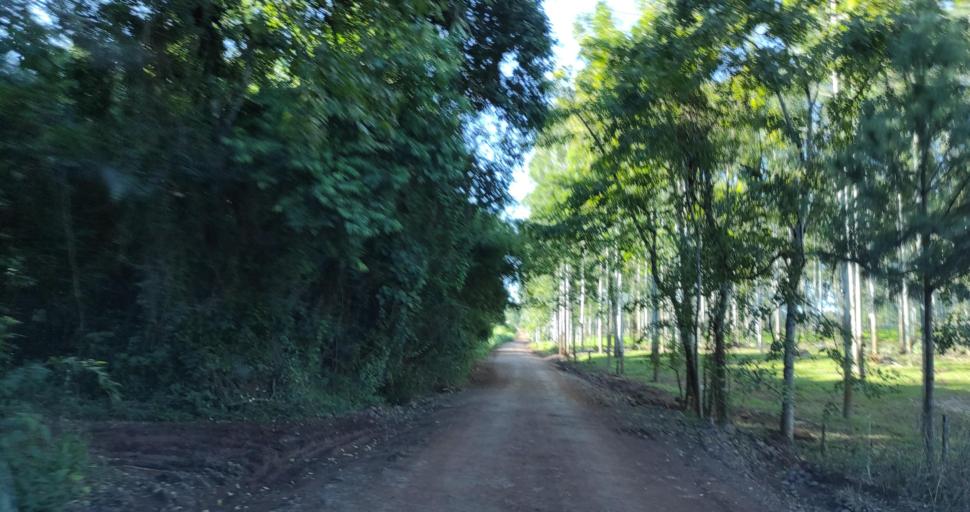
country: AR
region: Misiones
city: Garuhape
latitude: -26.8739
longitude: -54.9956
